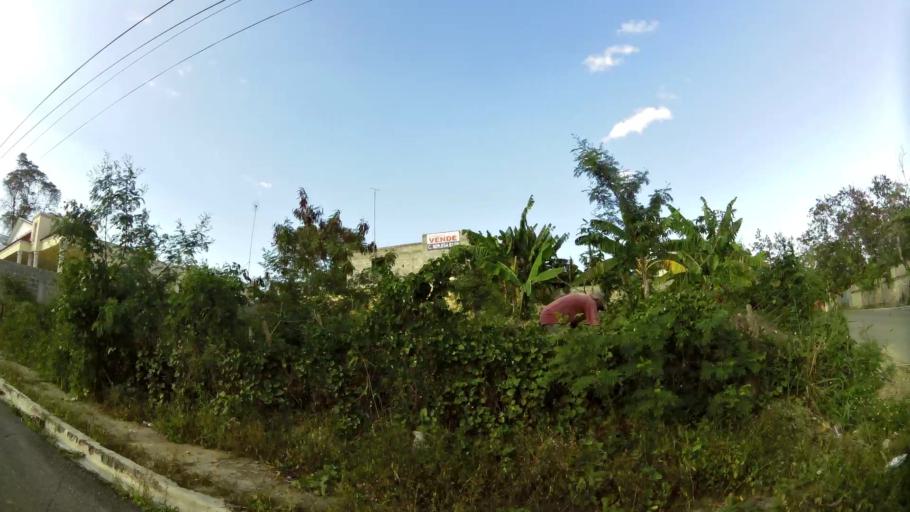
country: DO
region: Nacional
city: Ensanche Luperon
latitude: 18.5466
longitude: -69.9121
